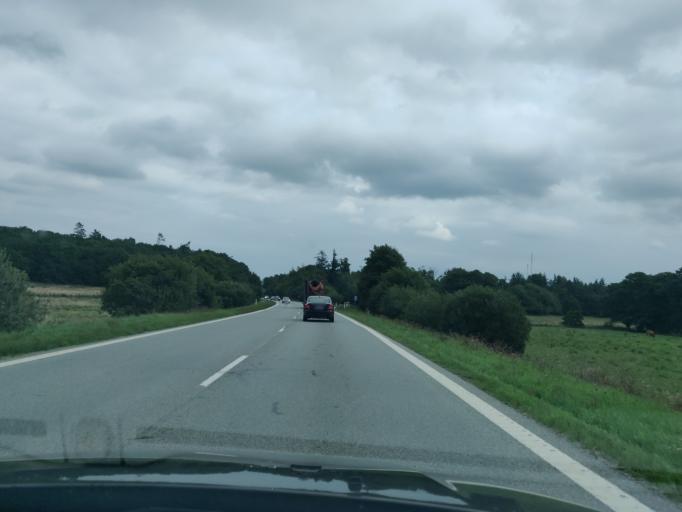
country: DK
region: North Denmark
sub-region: Alborg Kommune
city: Frejlev
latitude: 57.0102
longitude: 9.7817
